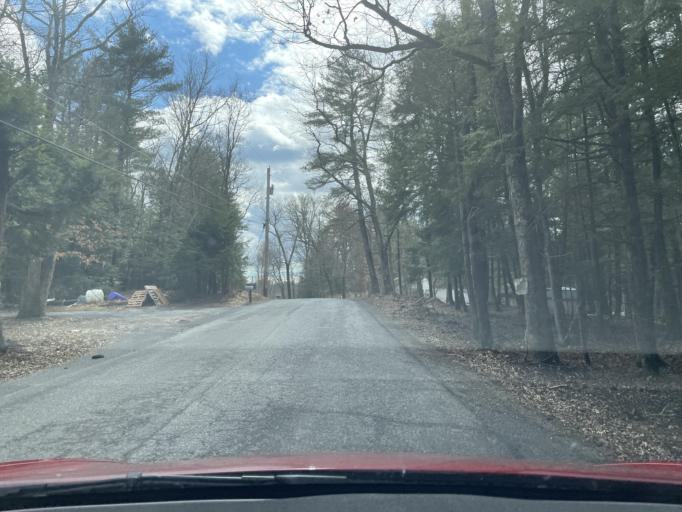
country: US
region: New York
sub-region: Ulster County
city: Zena
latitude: 42.0582
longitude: -74.0396
